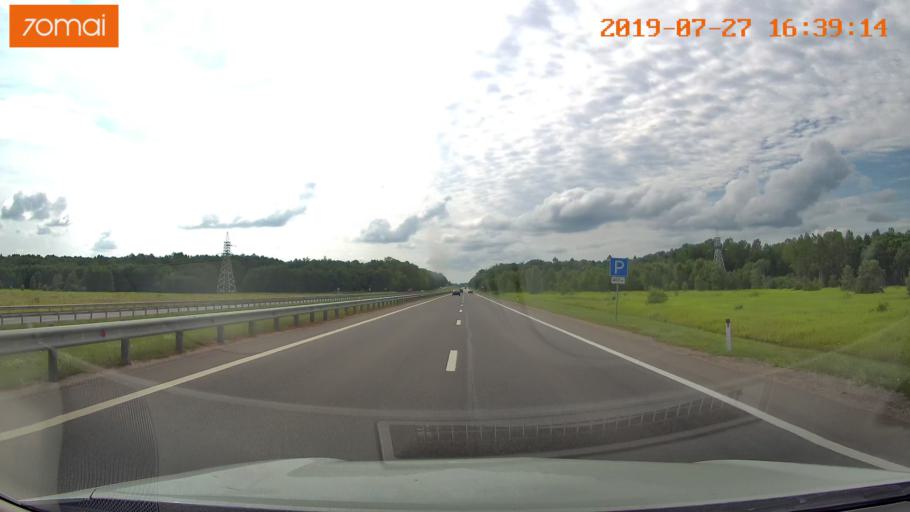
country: RU
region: Kaliningrad
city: Gvardeysk
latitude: 54.6492
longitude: 21.2060
